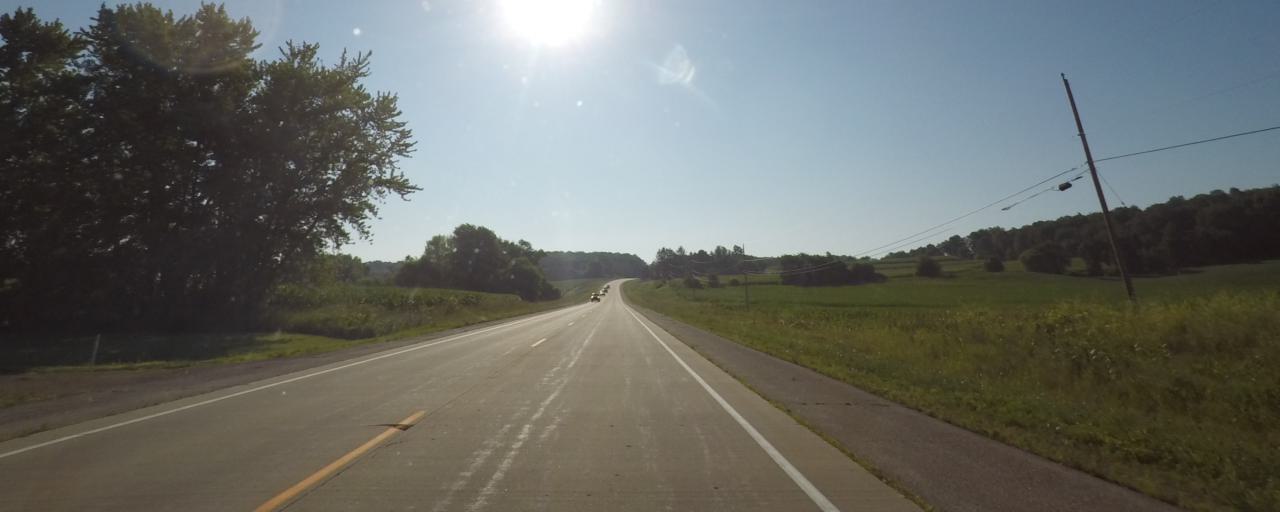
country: US
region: Wisconsin
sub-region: Jefferson County
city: Lake Ripley
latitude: 42.9739
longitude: -88.9422
